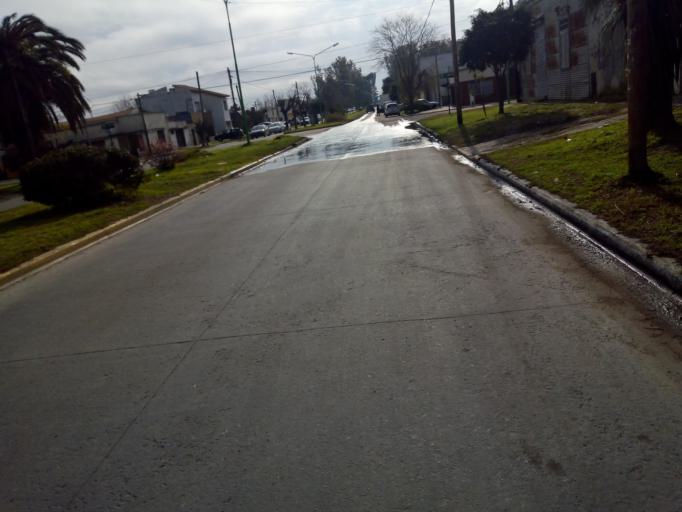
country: AR
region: Buenos Aires
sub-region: Partido de La Plata
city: La Plata
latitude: -34.8980
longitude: -57.9339
